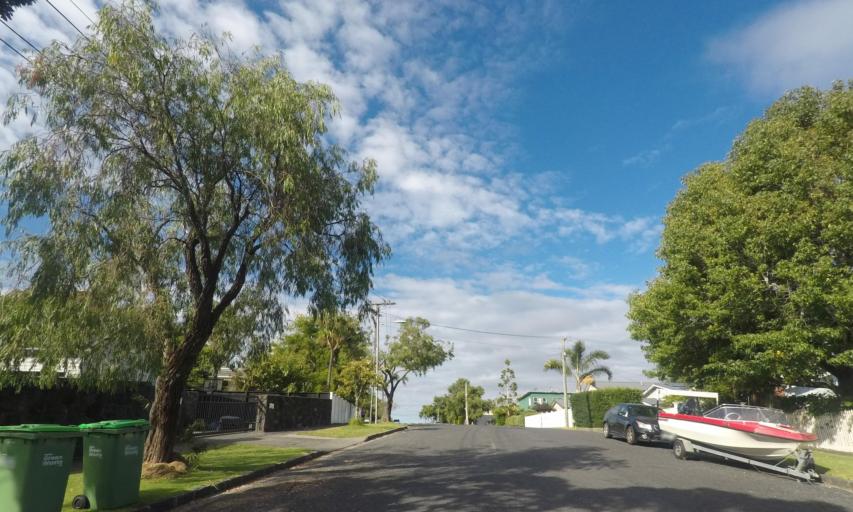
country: NZ
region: Auckland
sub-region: Auckland
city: Auckland
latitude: -36.8841
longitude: 174.7443
